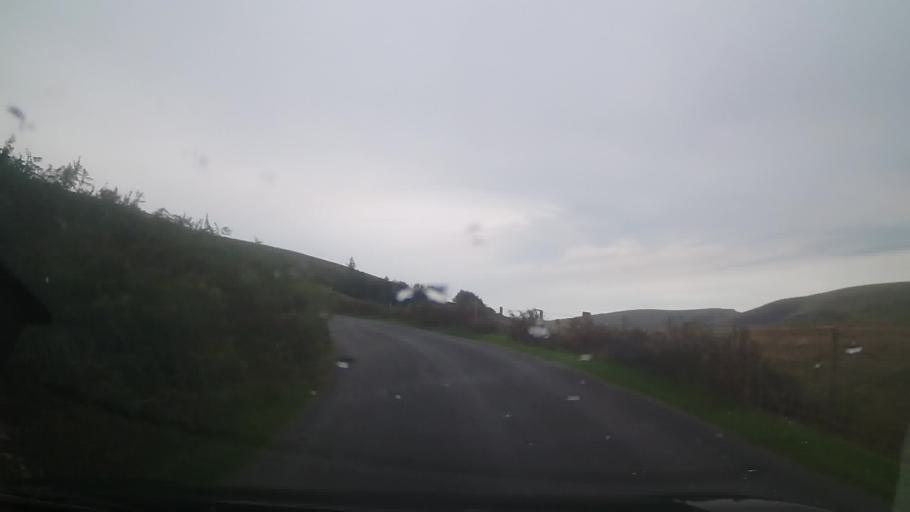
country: GB
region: Wales
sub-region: Sir Powys
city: Rhayader
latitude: 52.3086
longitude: -3.6353
